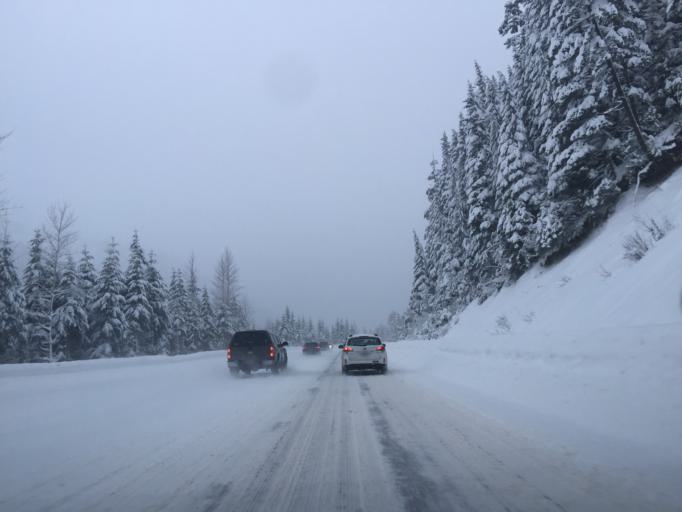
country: US
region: Washington
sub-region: Chelan County
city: Leavenworth
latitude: 47.7275
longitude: -121.1372
